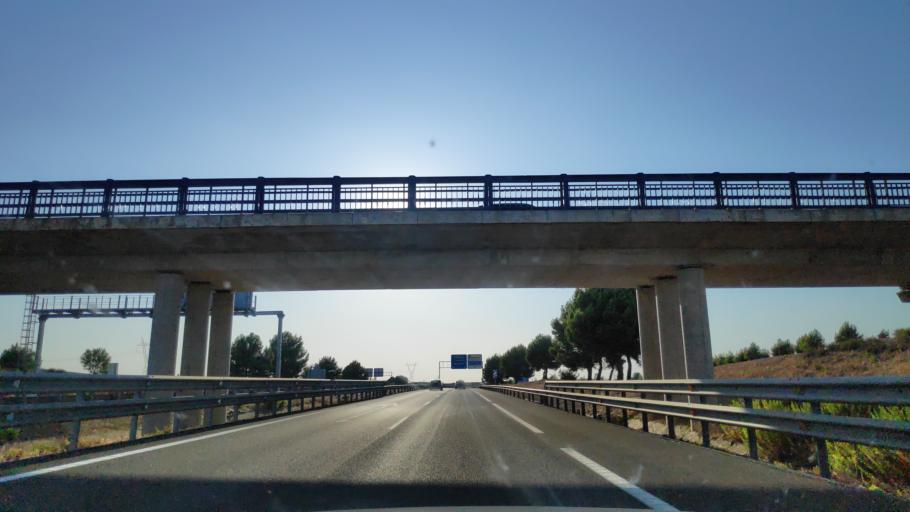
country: ES
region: Castille-La Mancha
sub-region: Provincia de Cuenca
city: Tarancon
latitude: 39.9949
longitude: -3.0085
